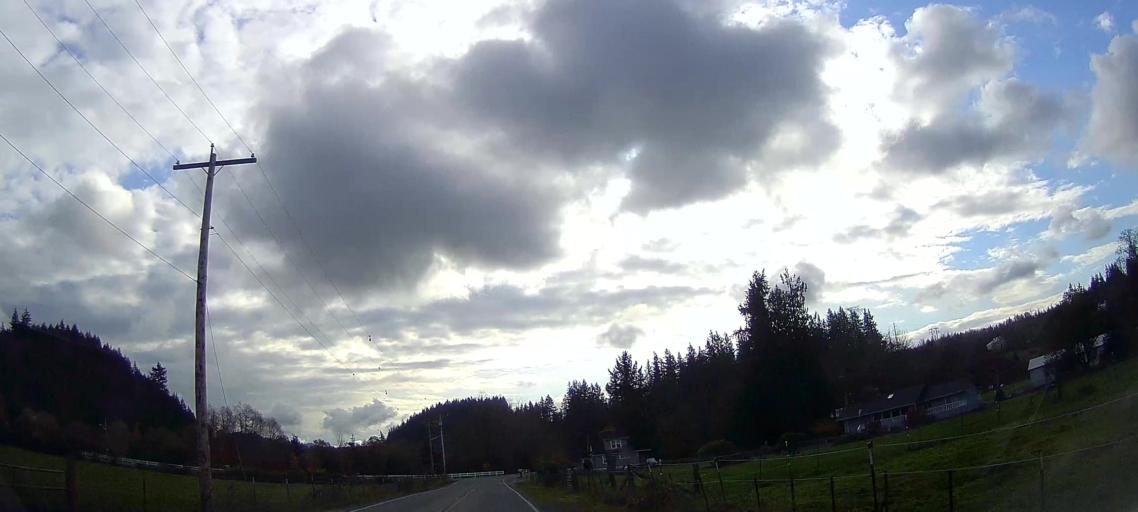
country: US
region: Washington
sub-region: Skagit County
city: Big Lake
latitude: 48.4255
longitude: -122.2095
